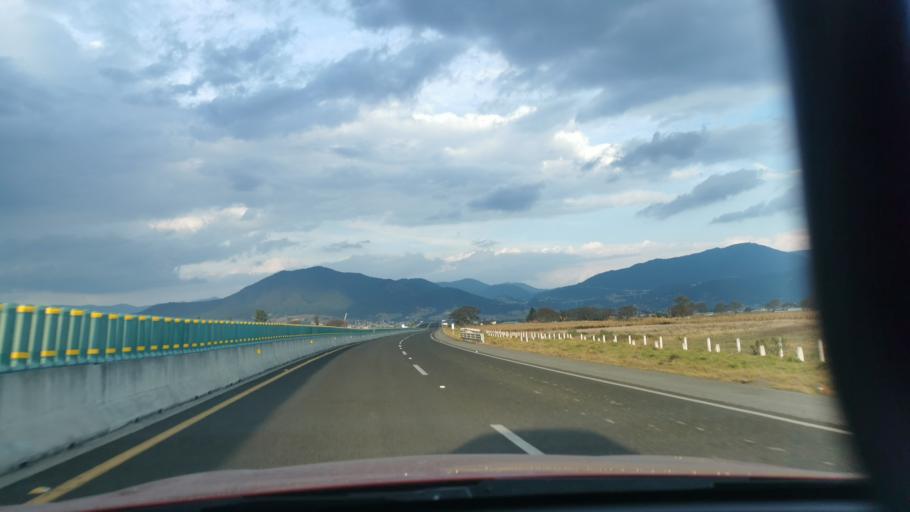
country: MX
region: Mexico
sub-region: Lerma
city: Colonia Agricola Analco
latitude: 19.3383
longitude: -99.5077
